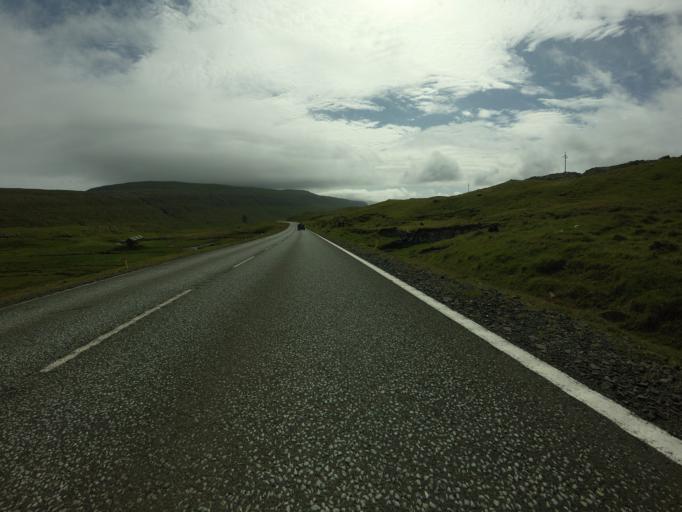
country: FO
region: Sandoy
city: Sandur
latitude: 61.8721
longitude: -6.8527
